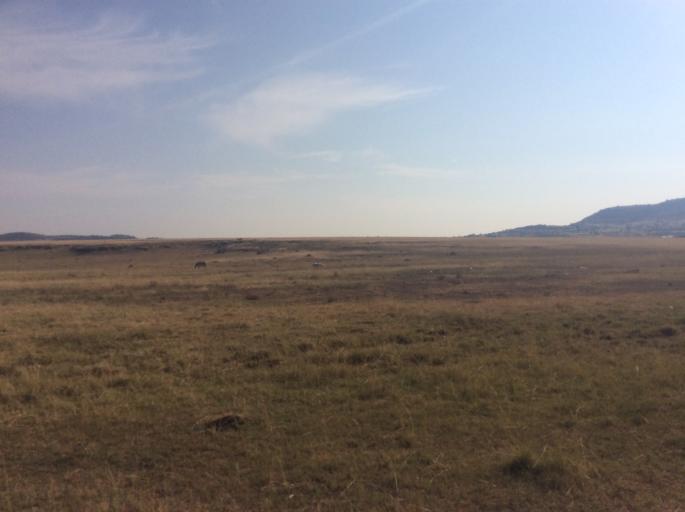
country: LS
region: Mafeteng
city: Mafeteng
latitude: -29.7144
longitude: 27.0079
